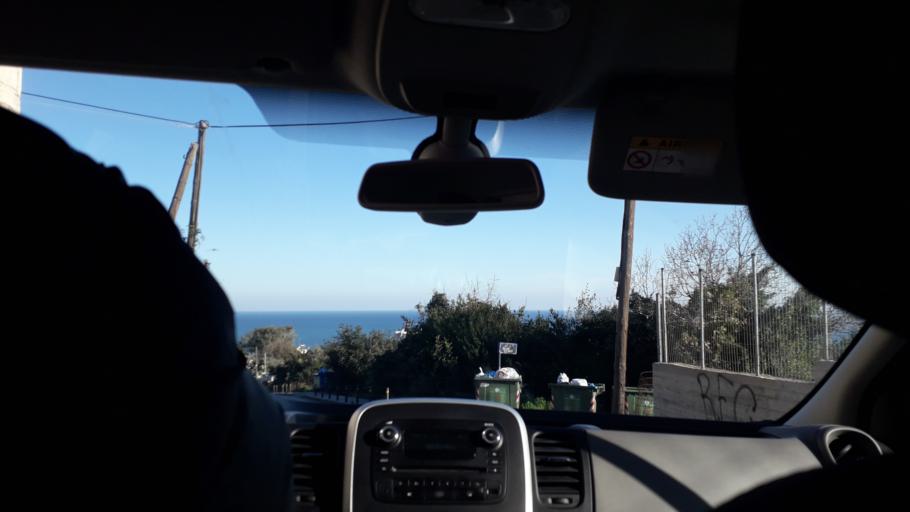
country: GR
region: Crete
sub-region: Nomos Rethymnis
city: Atsipopoulon
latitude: 35.3599
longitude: 24.4424
